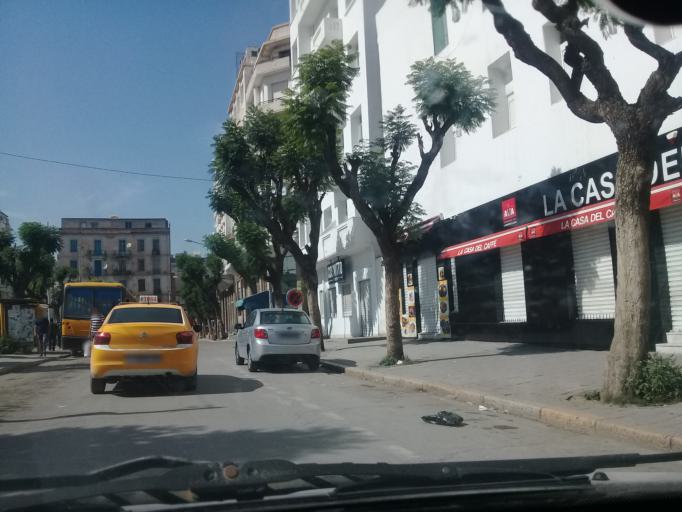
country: TN
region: Tunis
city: Tunis
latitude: 36.7963
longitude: 10.1813
